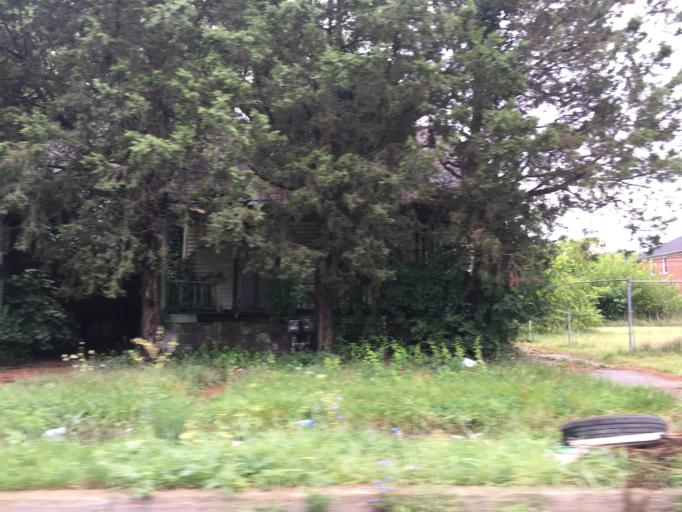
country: US
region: Michigan
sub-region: Wayne County
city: Highland Park
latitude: 42.4035
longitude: -83.1524
